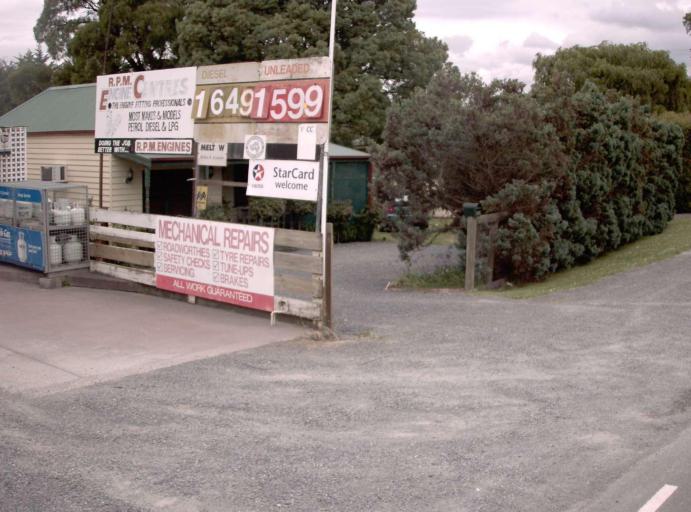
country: AU
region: Victoria
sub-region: Yarra Ranges
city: Mount Evelyn
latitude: -37.7797
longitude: 145.4278
